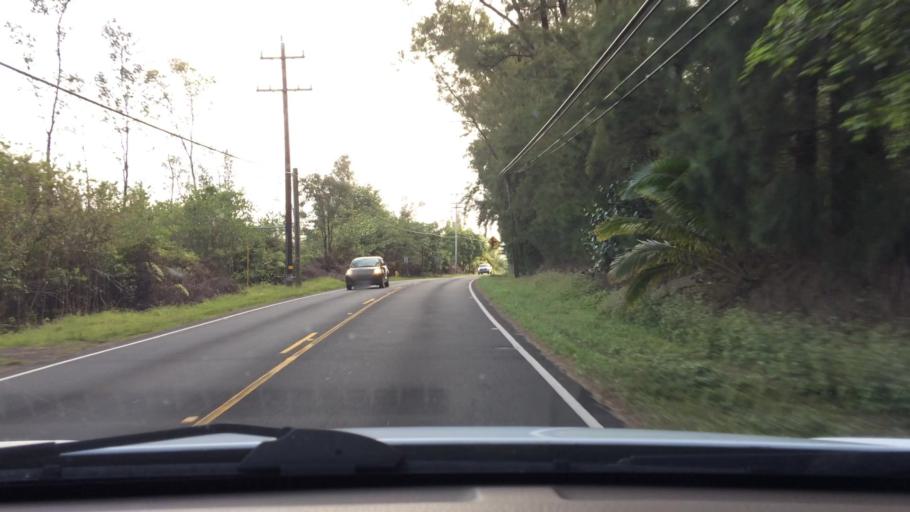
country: US
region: Hawaii
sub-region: Hawaii County
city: Hawaiian Paradise Park
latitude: 19.5057
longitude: -154.9508
